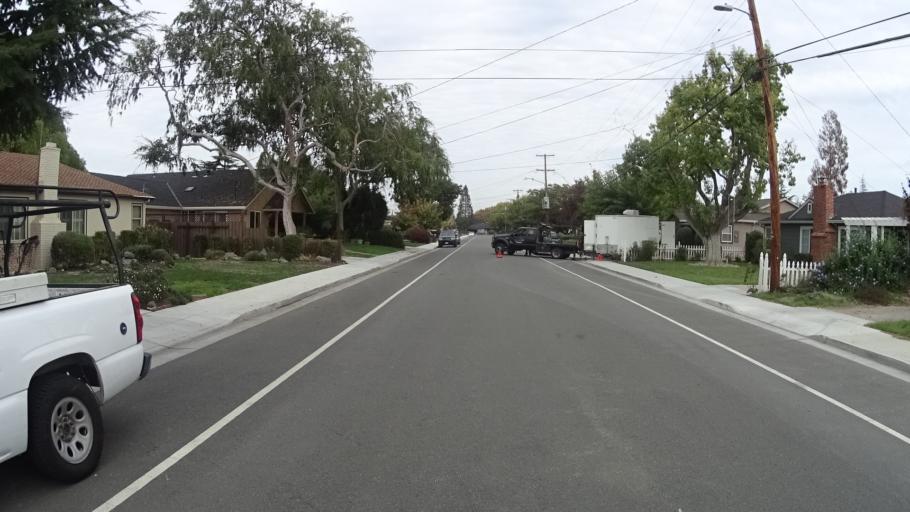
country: US
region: California
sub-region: Santa Clara County
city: Burbank
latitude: 37.3249
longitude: -121.9575
